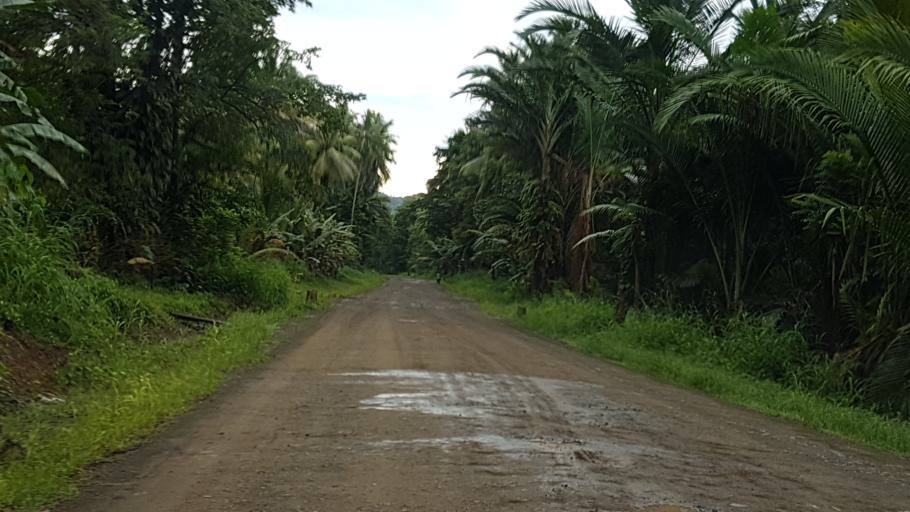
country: PG
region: Milne Bay
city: Alotau
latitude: -10.3425
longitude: 150.5983
